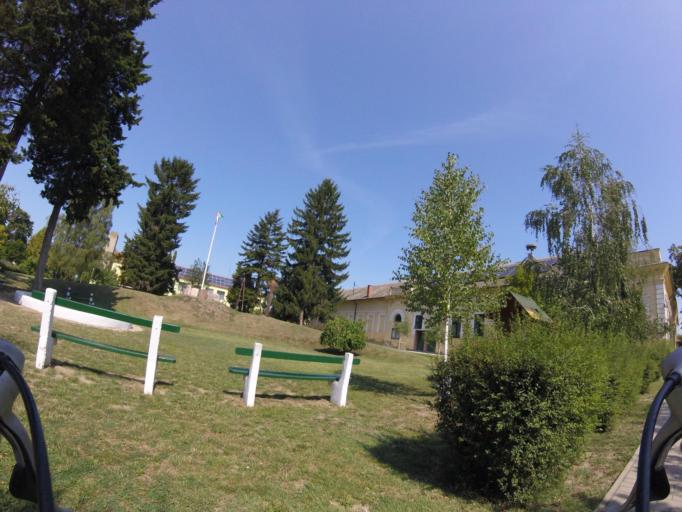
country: HU
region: Bacs-Kiskun
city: Madaras
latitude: 46.0590
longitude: 19.2603
